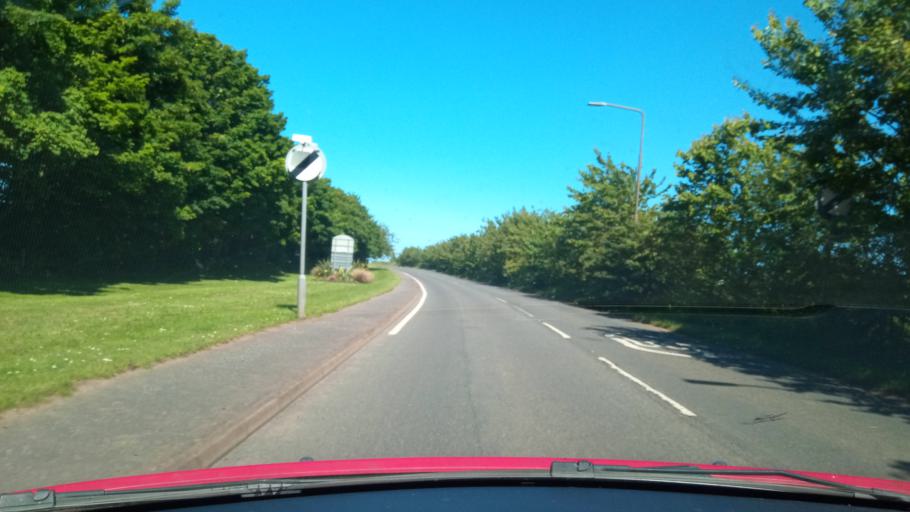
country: GB
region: Scotland
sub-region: East Lothian
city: North Berwick
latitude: 56.0547
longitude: -2.6945
